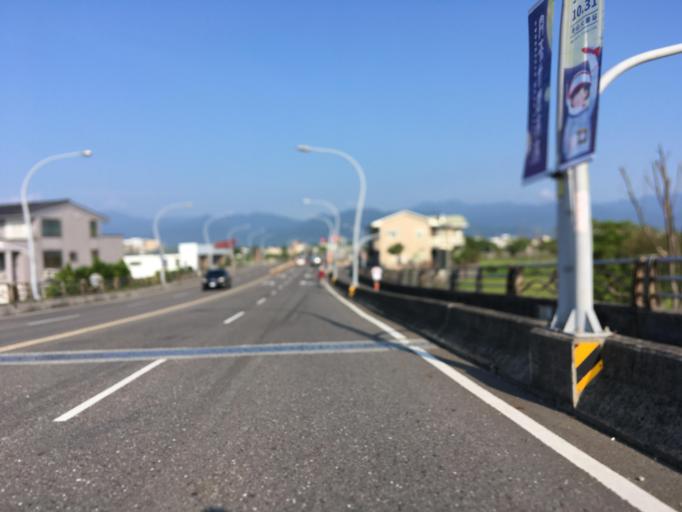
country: TW
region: Taiwan
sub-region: Yilan
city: Yilan
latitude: 24.6843
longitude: 121.7450
